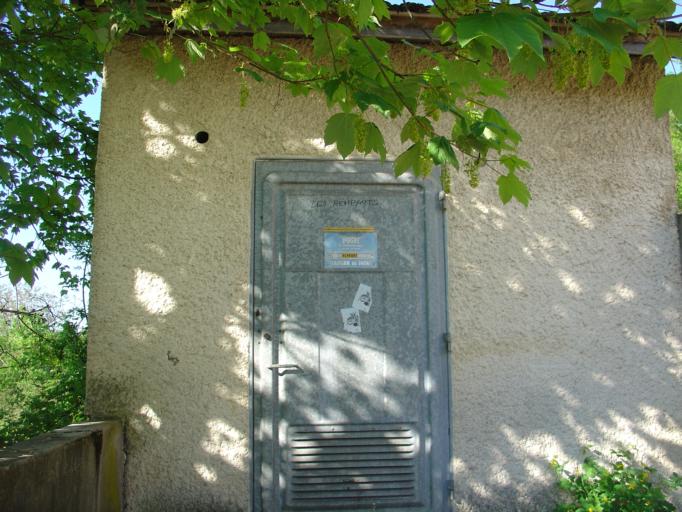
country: FR
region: Lorraine
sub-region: Departement de Meurthe-et-Moselle
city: Foug
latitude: 48.6847
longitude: 5.7848
